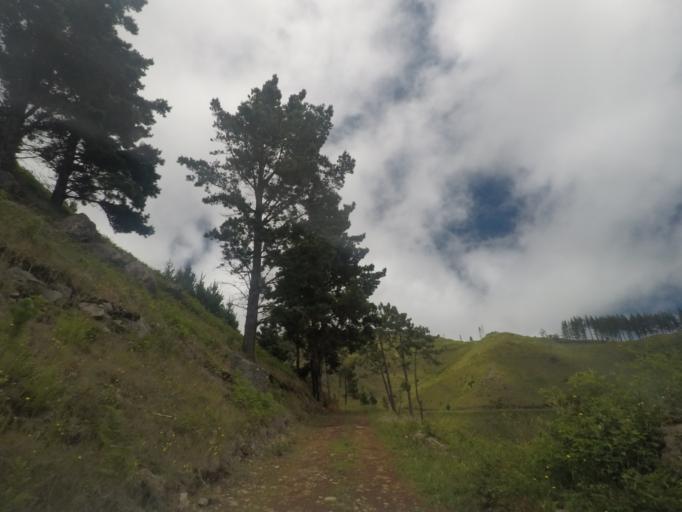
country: PT
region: Madeira
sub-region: Funchal
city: Nossa Senhora do Monte
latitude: 32.7022
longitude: -16.9050
